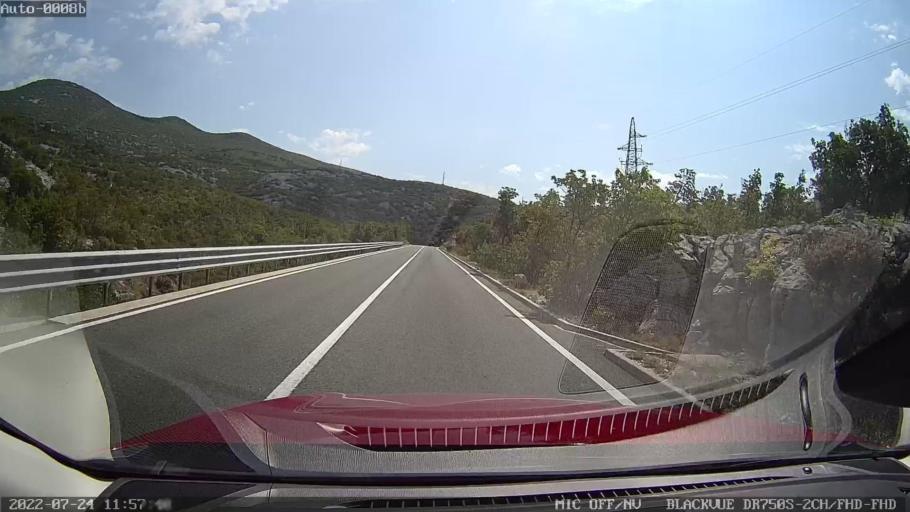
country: HR
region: Primorsko-Goranska
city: Novi Vinodolski
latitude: 45.1198
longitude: 14.8444
